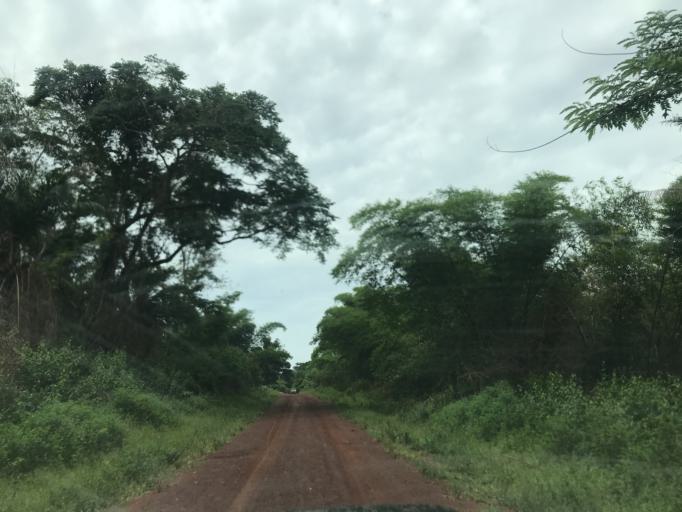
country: CD
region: Eastern Province
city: Buta
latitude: 2.3439
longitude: 24.9573
